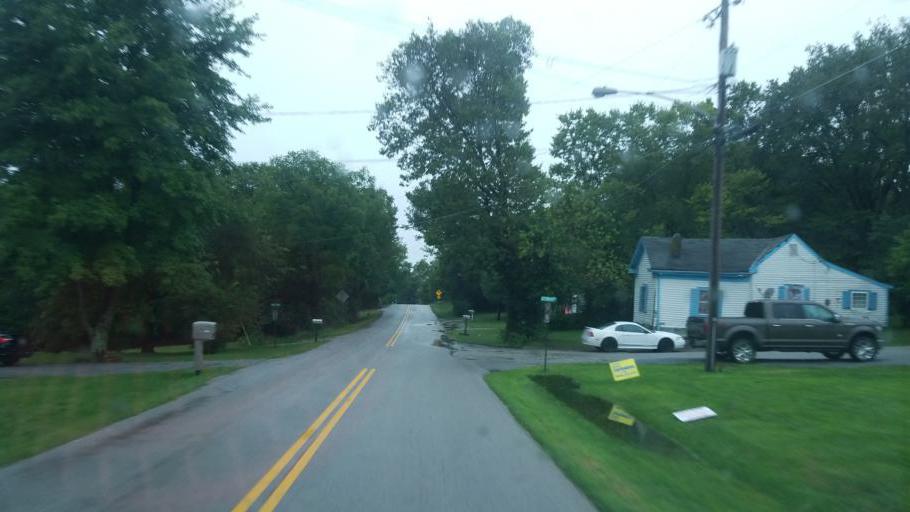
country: US
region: Kentucky
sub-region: Fleming County
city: Flemingsburg
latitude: 38.4269
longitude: -83.7220
